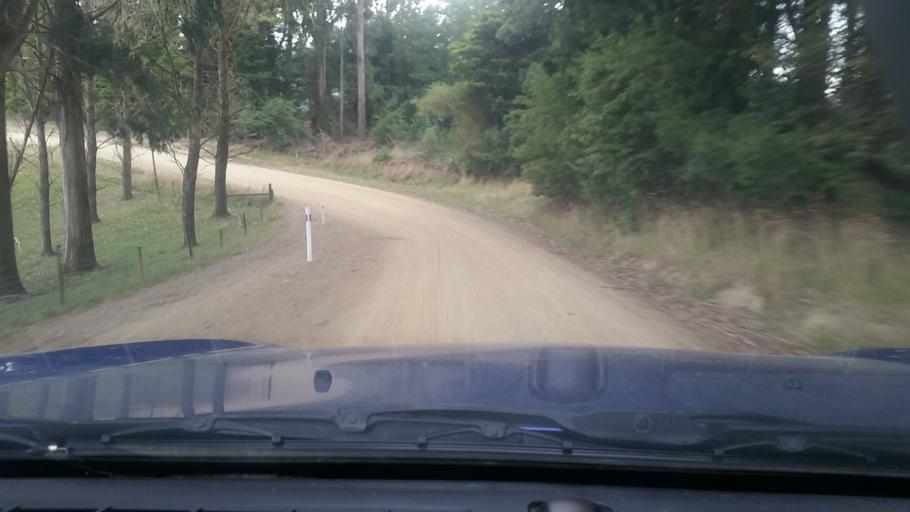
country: NZ
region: Otago
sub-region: Clutha District
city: Balclutha
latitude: -45.6797
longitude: 169.4979
